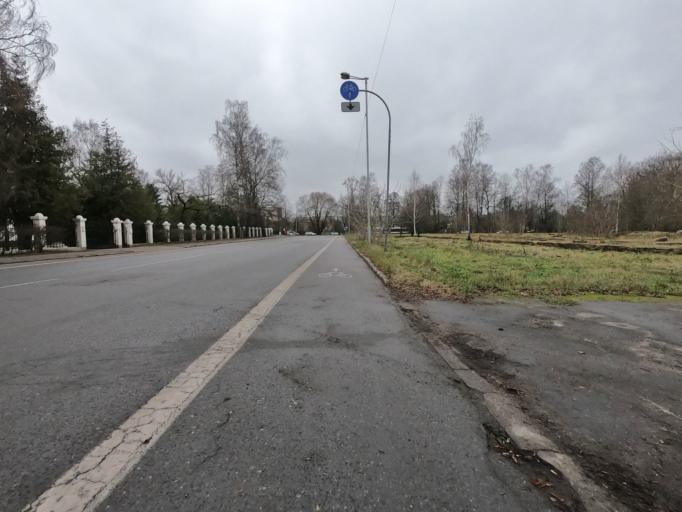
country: LV
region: Marupe
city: Marupe
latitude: 56.9535
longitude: 24.0235
